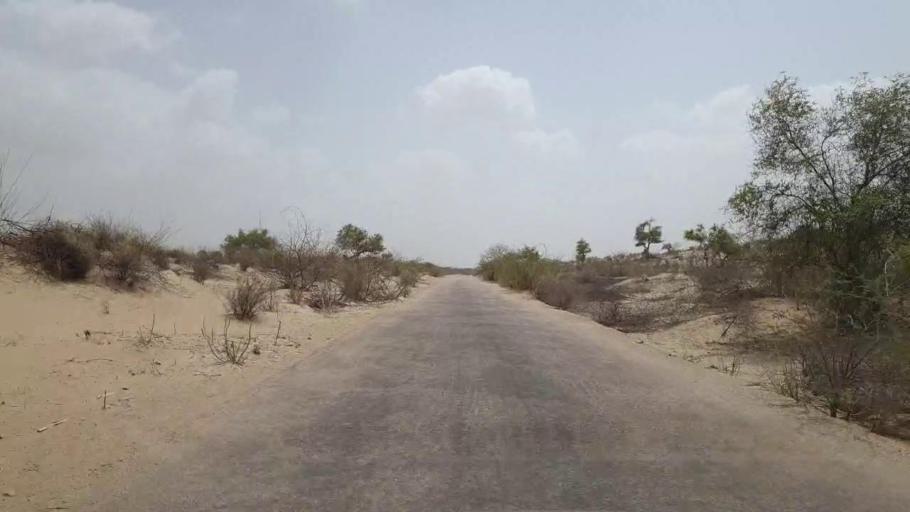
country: PK
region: Sindh
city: Diplo
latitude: 24.3726
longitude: 69.4118
